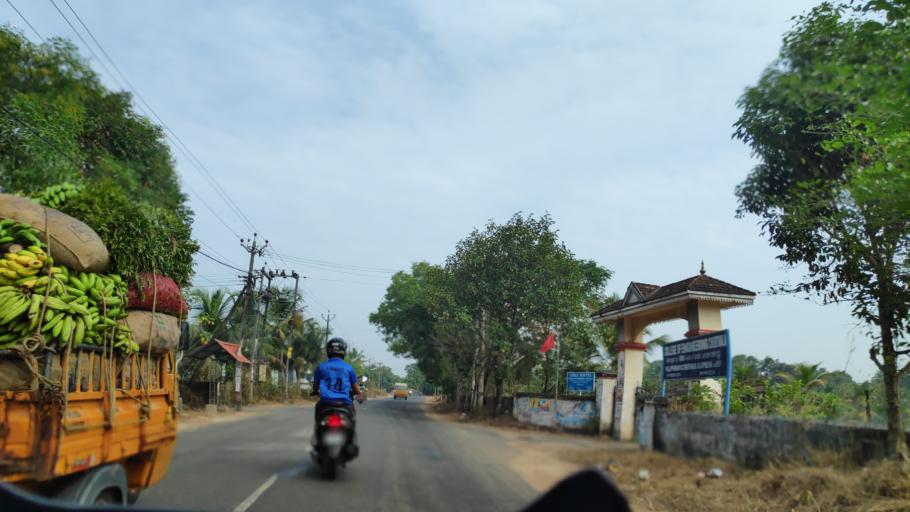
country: IN
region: Kerala
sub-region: Kottayam
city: Vaikam
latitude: 9.7571
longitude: 76.3627
